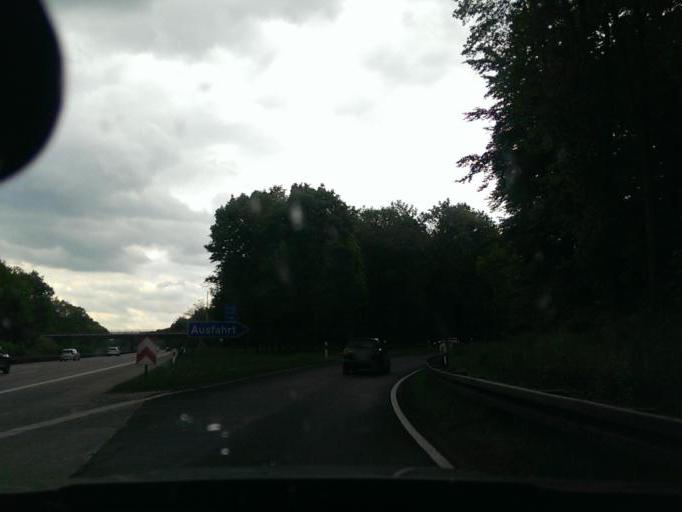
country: DE
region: Lower Saxony
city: Laatzen
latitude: 52.3123
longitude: 9.8685
